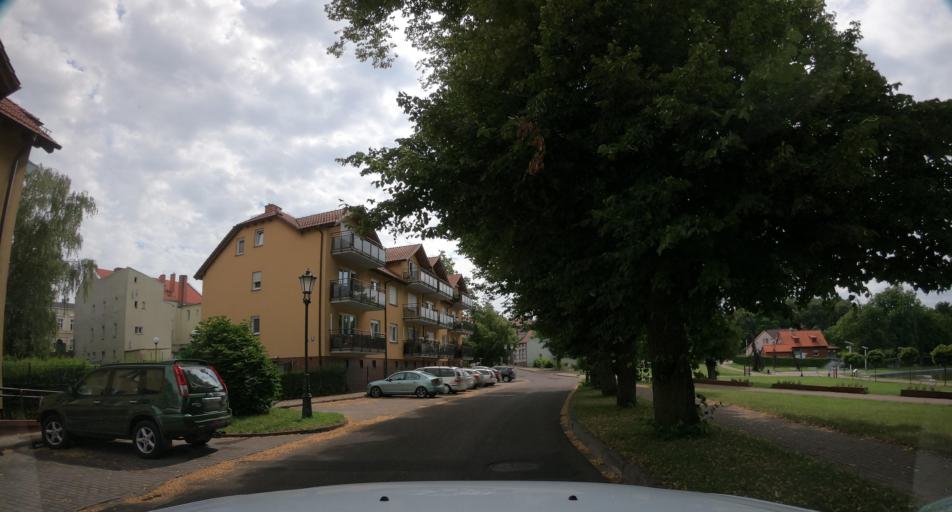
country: PL
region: West Pomeranian Voivodeship
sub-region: Powiat walecki
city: Walcz
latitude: 53.2696
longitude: 16.4635
